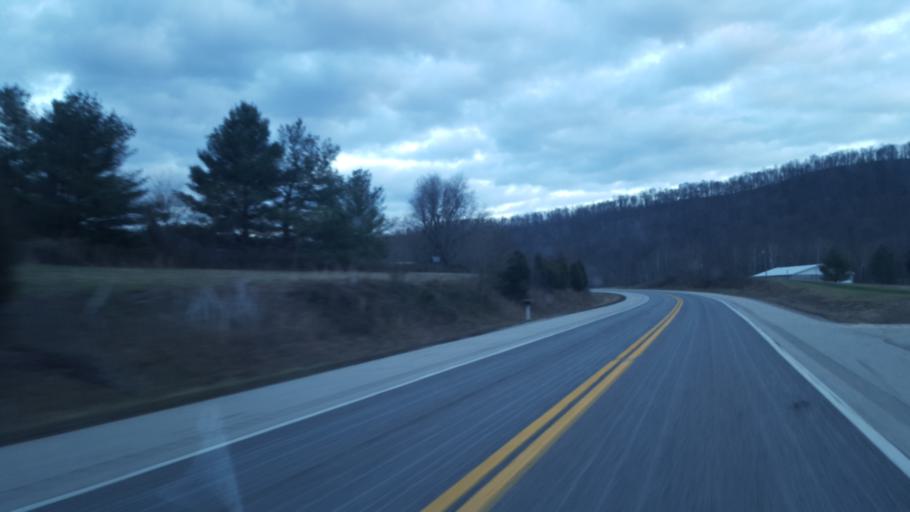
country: US
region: Kentucky
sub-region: Lewis County
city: Vanceburg
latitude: 38.5834
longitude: -83.3658
